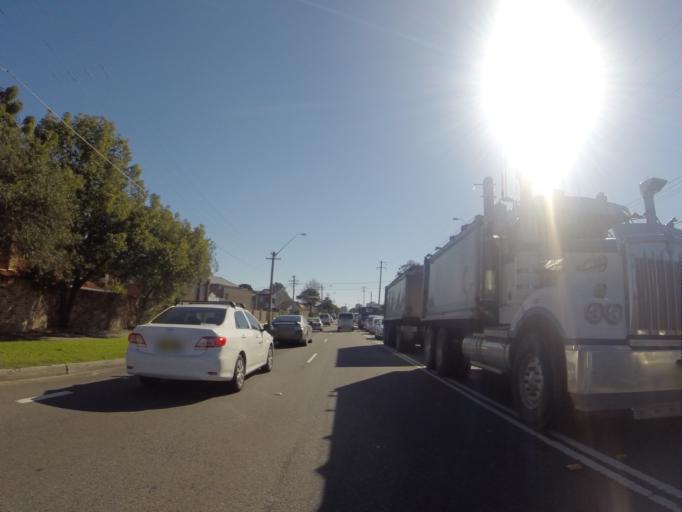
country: AU
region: New South Wales
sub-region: Kogarah
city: Hurstville Grove
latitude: -33.9763
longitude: 151.1038
